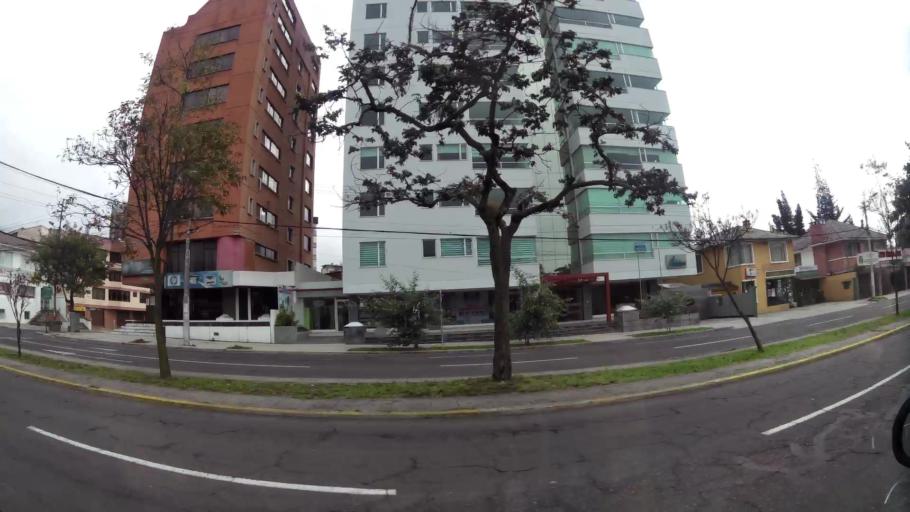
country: EC
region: Pichincha
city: Quito
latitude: -0.1960
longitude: -78.4919
